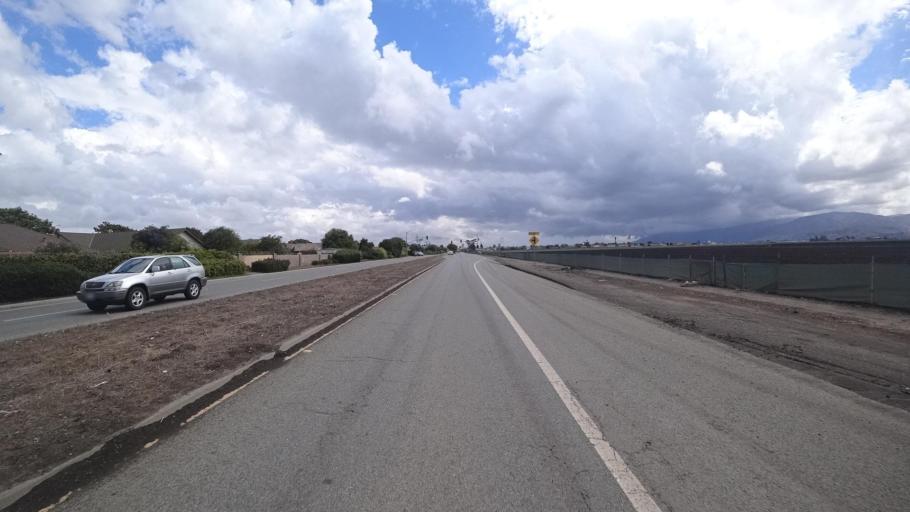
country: US
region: California
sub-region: Monterey County
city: Salinas
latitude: 36.6637
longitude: -121.6802
